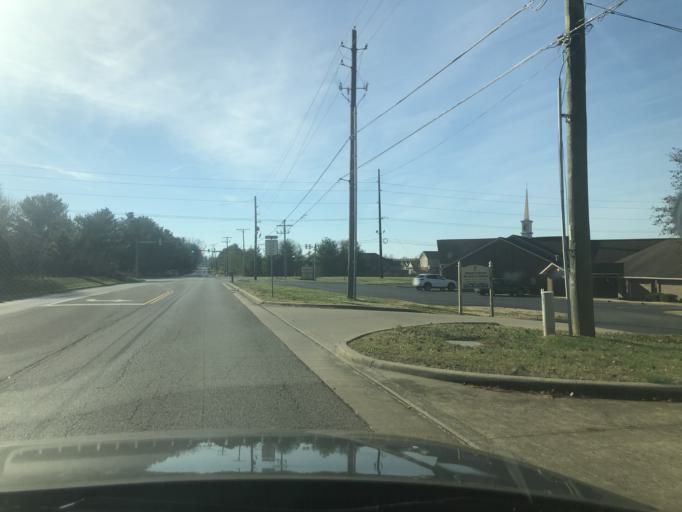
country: US
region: Indiana
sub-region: Warrick County
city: Newburgh
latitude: 37.9706
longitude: -87.4412
